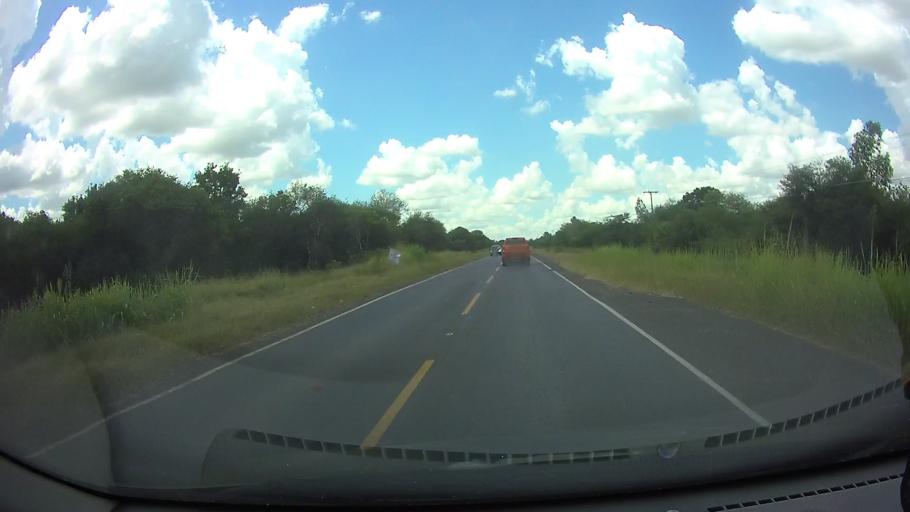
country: PY
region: Presidente Hayes
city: Nanawa
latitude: -25.1999
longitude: -57.6406
